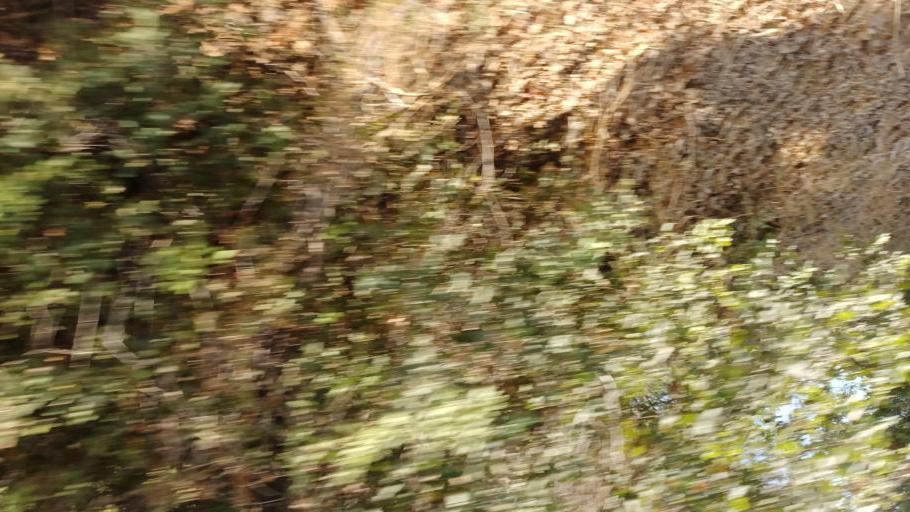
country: CY
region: Pafos
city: Polis
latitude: 34.9722
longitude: 32.4231
